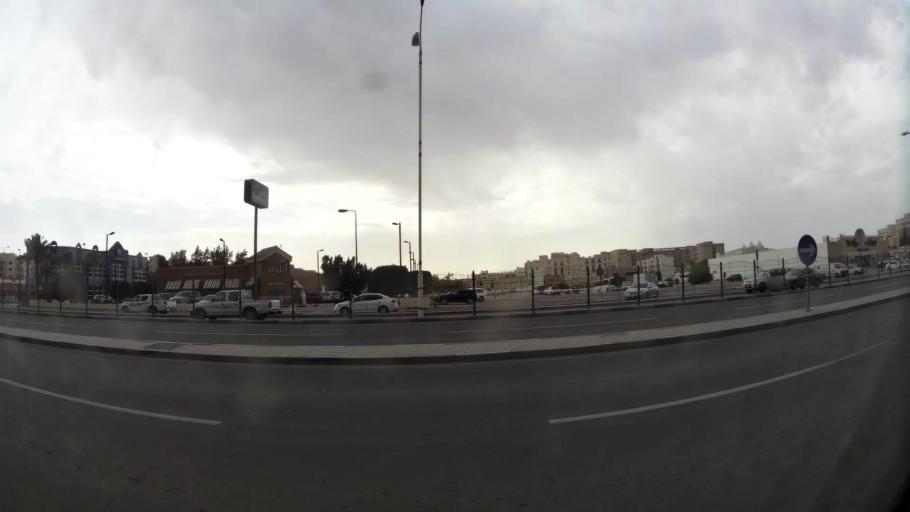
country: QA
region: Baladiyat ad Dawhah
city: Doha
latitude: 25.2778
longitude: 51.5080
